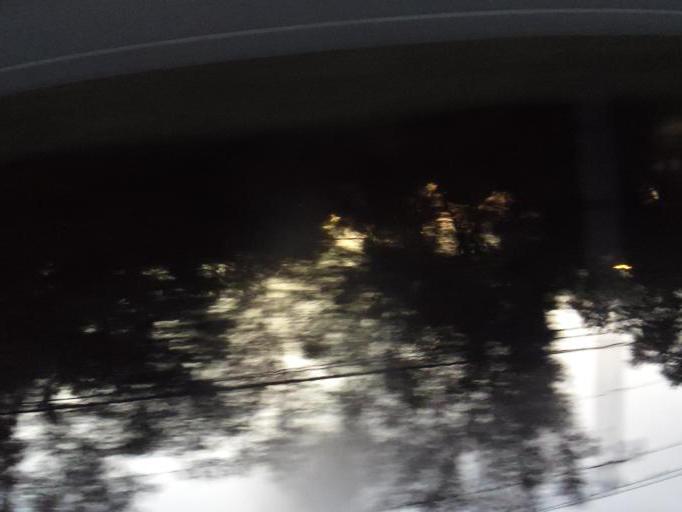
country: US
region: Florida
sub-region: Saint Johns County
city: Saint Augustine Shores
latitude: 29.8218
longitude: -81.3474
